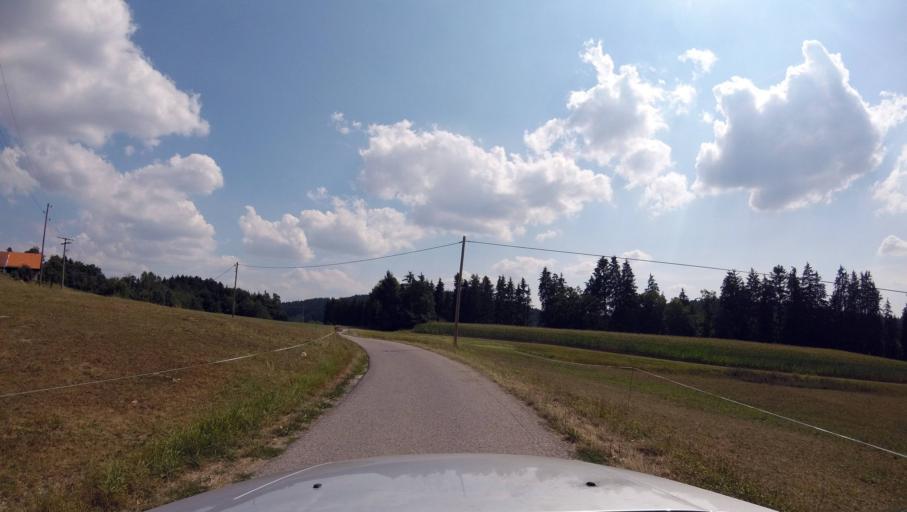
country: DE
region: Baden-Wuerttemberg
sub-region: Regierungsbezirk Stuttgart
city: Alfdorf
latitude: 48.8648
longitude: 9.7203
